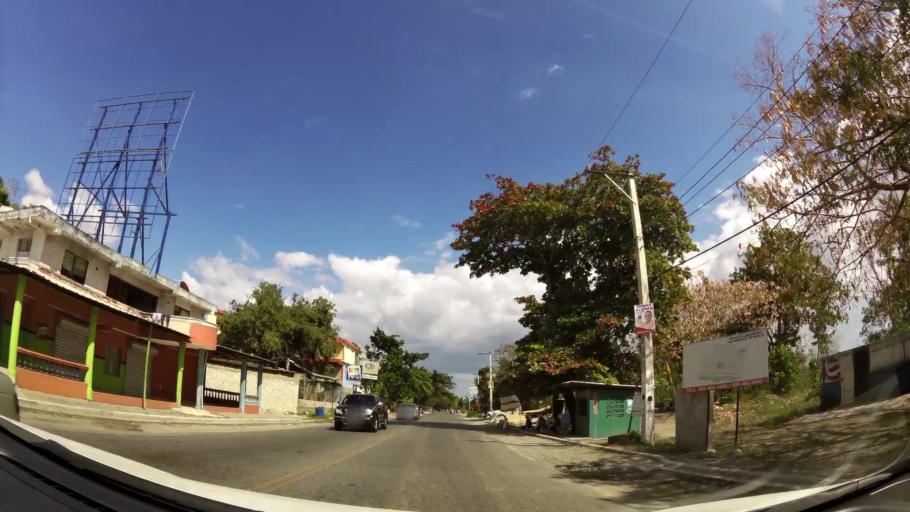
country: DO
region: San Cristobal
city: San Cristobal
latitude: 18.4281
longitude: -70.0807
